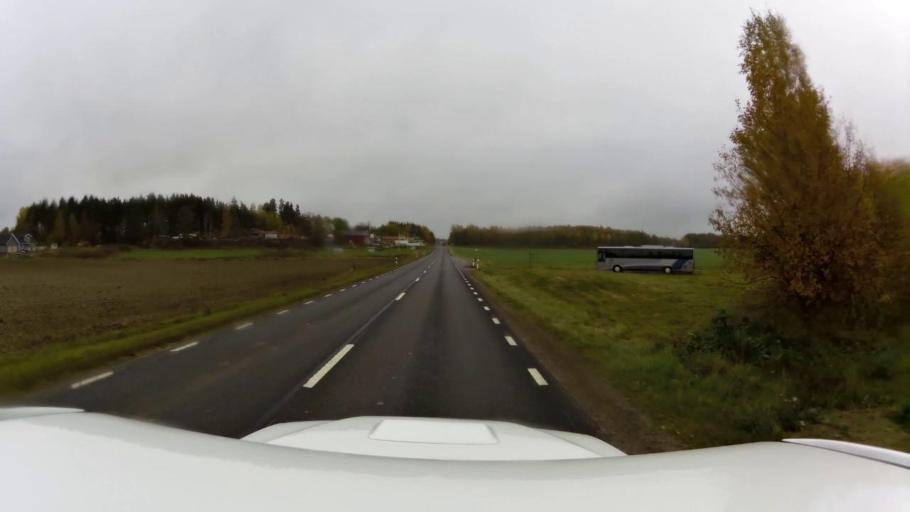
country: SE
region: OEstergoetland
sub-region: Linkopings Kommun
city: Linghem
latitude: 58.3821
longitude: 15.7924
